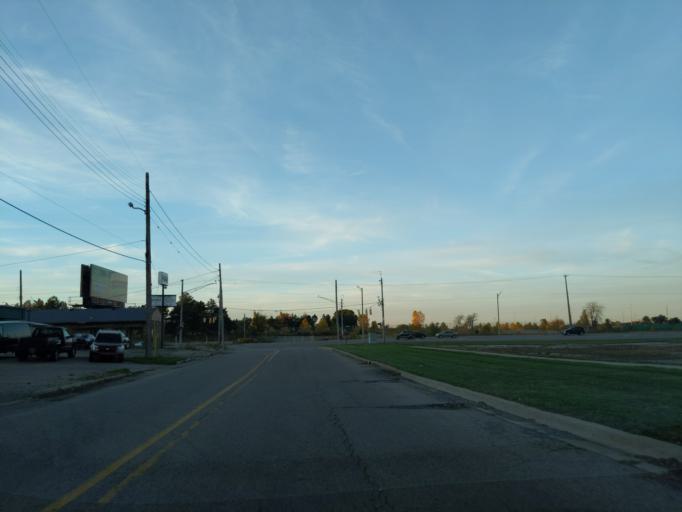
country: US
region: Michigan
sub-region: Ingham County
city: Edgemont Park
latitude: 42.7400
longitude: -84.5875
